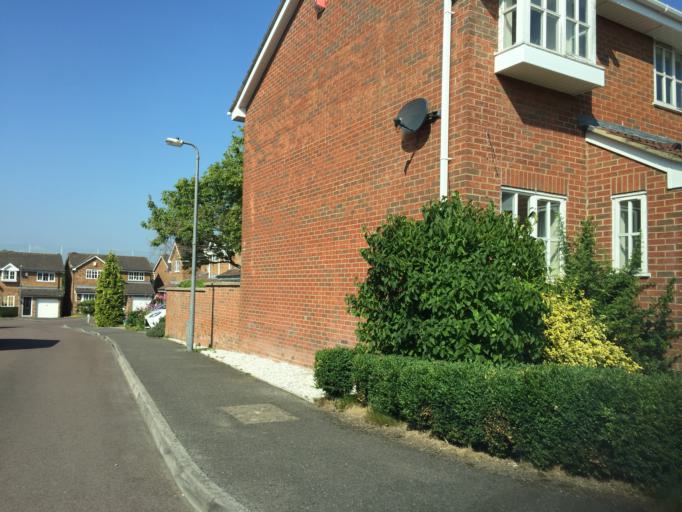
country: GB
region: England
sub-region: South Gloucestershire
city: Stoke Gifford
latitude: 51.5160
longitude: -2.5371
